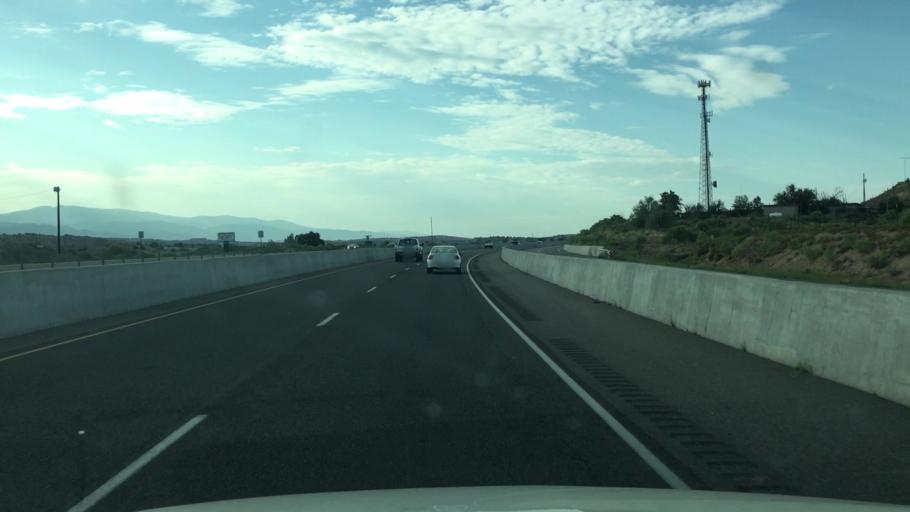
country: US
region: New Mexico
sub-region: Santa Fe County
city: El Valle de Arroyo Seco
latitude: 35.9567
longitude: -106.0231
